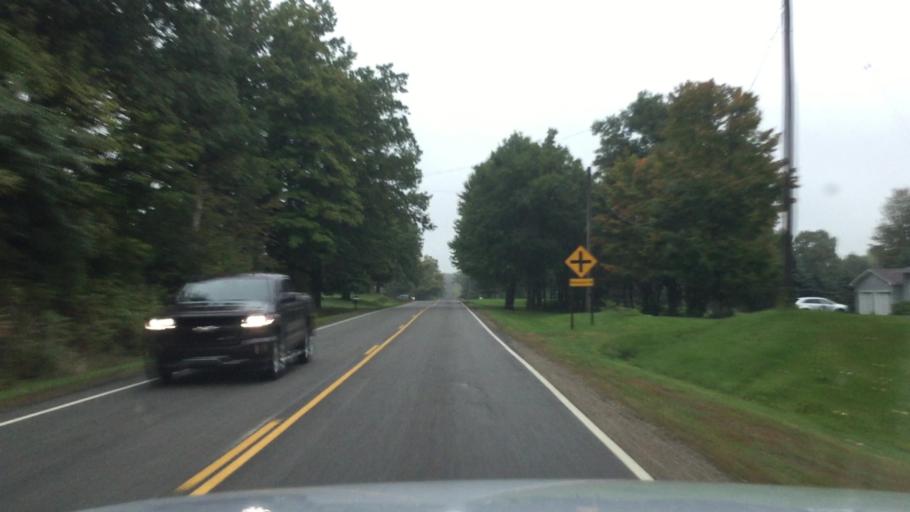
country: US
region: Michigan
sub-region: Shiawassee County
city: Corunna
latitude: 42.9358
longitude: -84.1244
